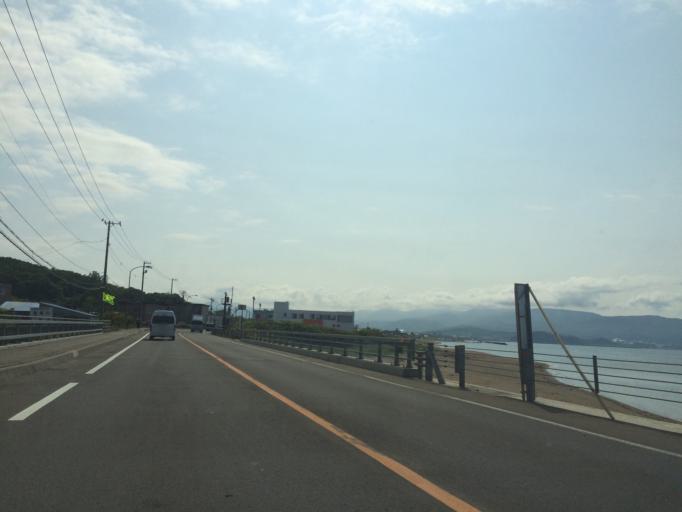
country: JP
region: Hokkaido
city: Yoichi
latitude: 43.1972
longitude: 140.8430
